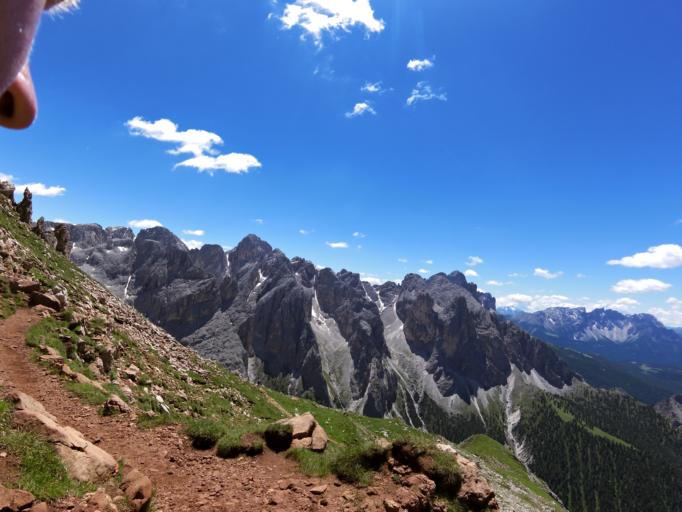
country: IT
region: Trentino-Alto Adige
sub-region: Bolzano
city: Siusi
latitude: 46.4975
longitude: 11.6131
